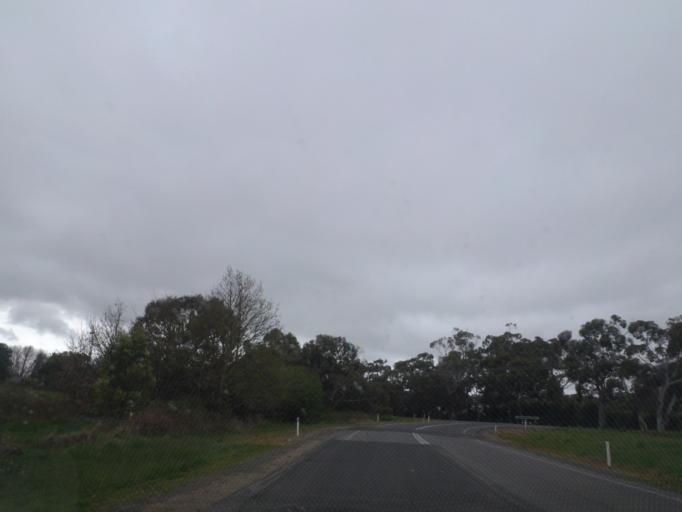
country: AU
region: Victoria
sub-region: Hume
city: Sunbury
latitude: -37.3265
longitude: 144.5870
